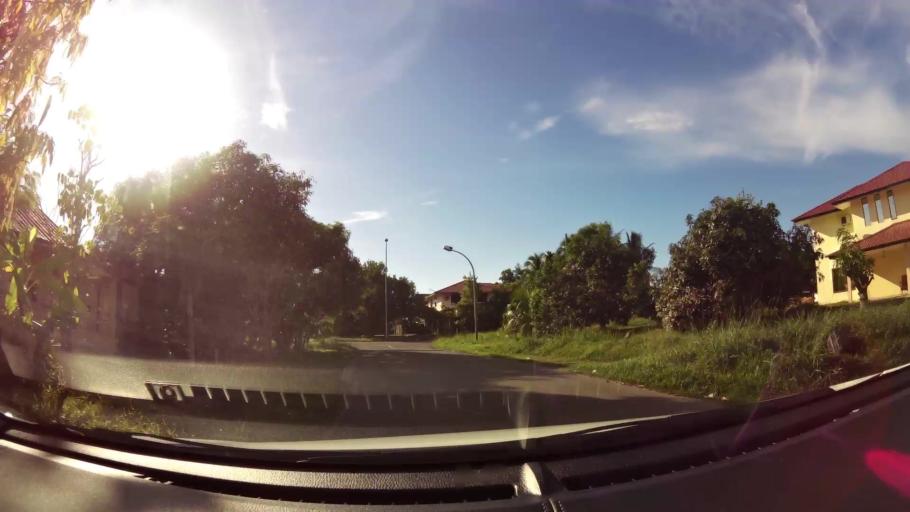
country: BN
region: Brunei and Muara
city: Bandar Seri Begawan
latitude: 4.9810
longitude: 114.9649
